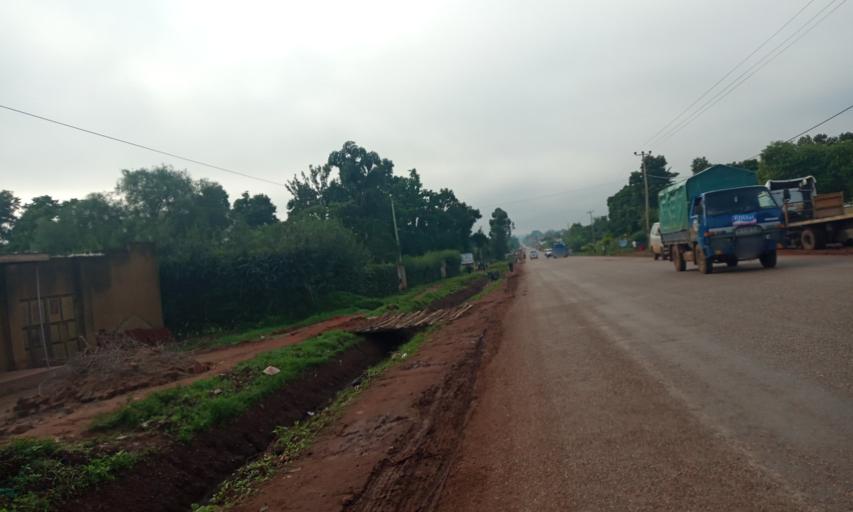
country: UG
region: Eastern Region
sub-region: Mbale District
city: Mbale
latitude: 1.1195
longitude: 34.1698
